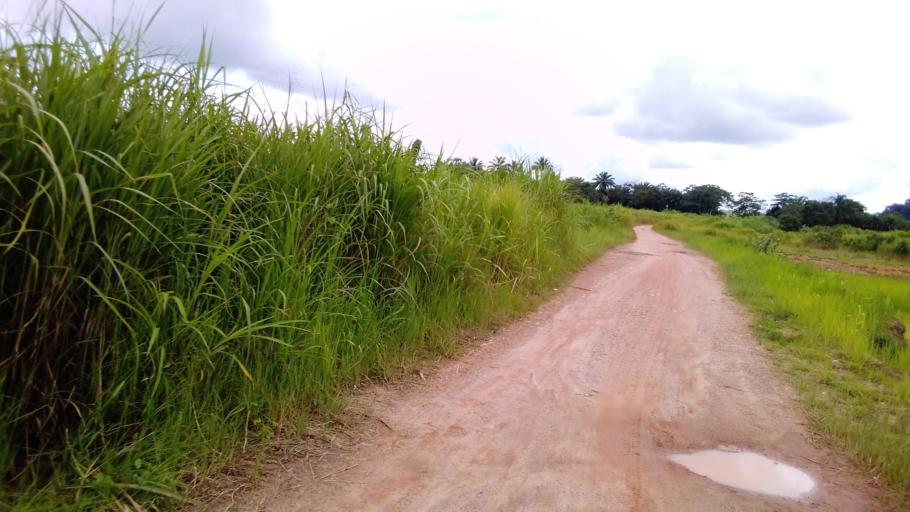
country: SL
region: Eastern Province
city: Koidu
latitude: 8.6808
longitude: -10.9612
